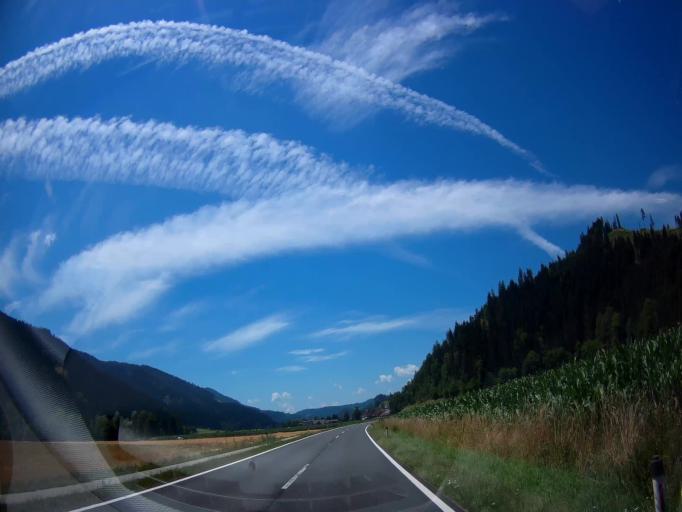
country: AT
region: Carinthia
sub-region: Politischer Bezirk Sankt Veit an der Glan
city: Micheldorf
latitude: 46.9030
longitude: 14.3953
